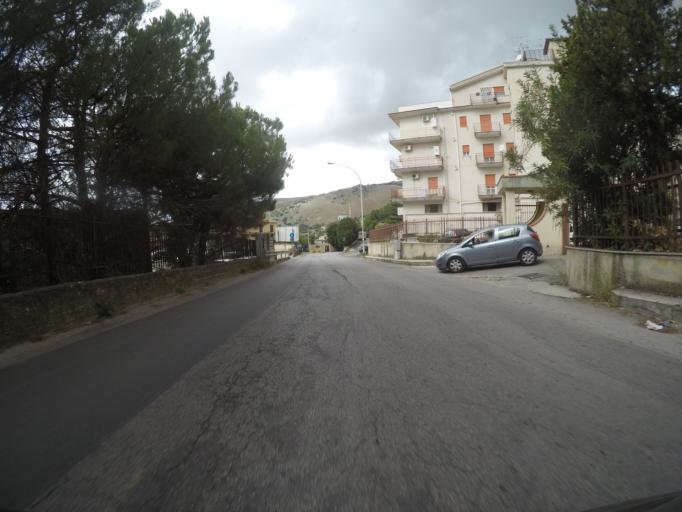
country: IT
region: Sicily
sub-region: Palermo
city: Montelepre
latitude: 38.0928
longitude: 13.1712
